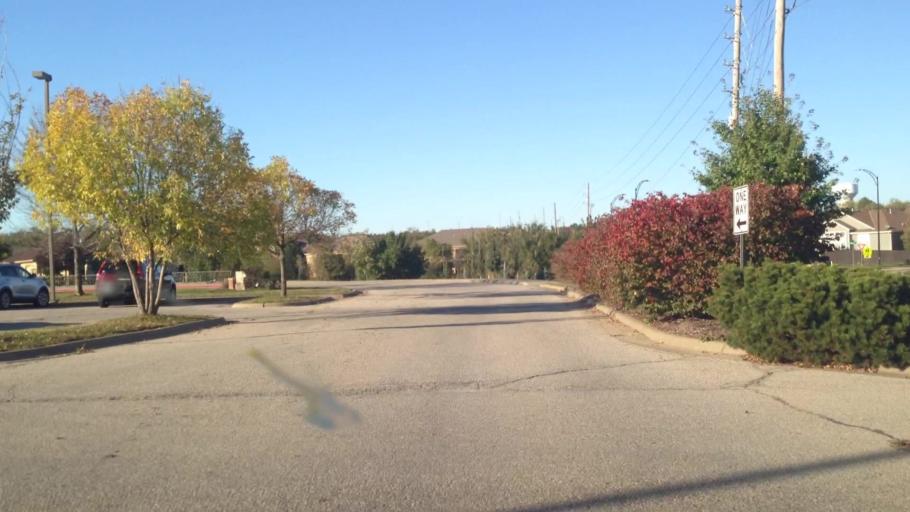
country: US
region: Kansas
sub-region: Douglas County
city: Lawrence
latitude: 38.9632
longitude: -95.3260
